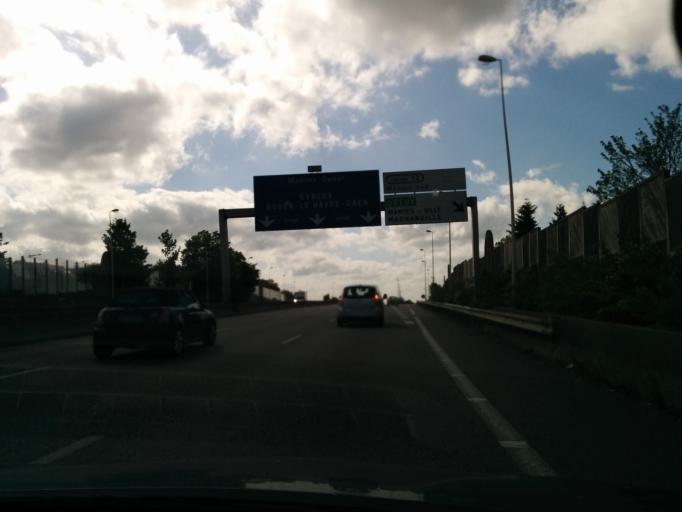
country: FR
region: Ile-de-France
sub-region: Departement des Yvelines
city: Mantes-la-Ville
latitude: 48.9795
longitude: 1.7029
